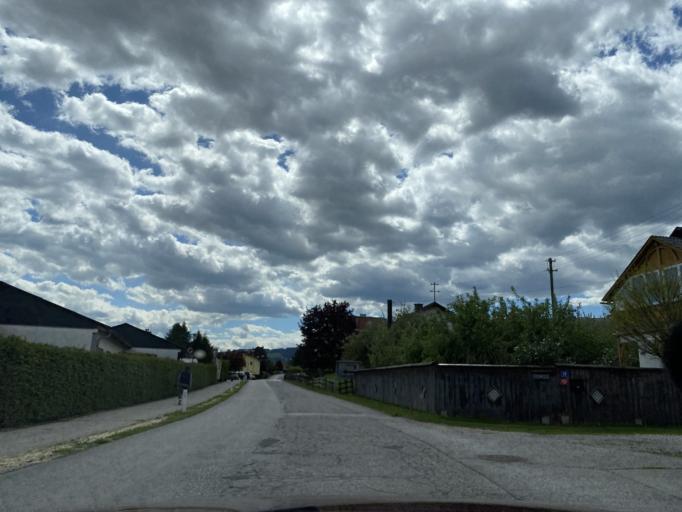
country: AT
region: Carinthia
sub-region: Politischer Bezirk Wolfsberg
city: Wolfsberg
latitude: 46.8304
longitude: 14.8352
